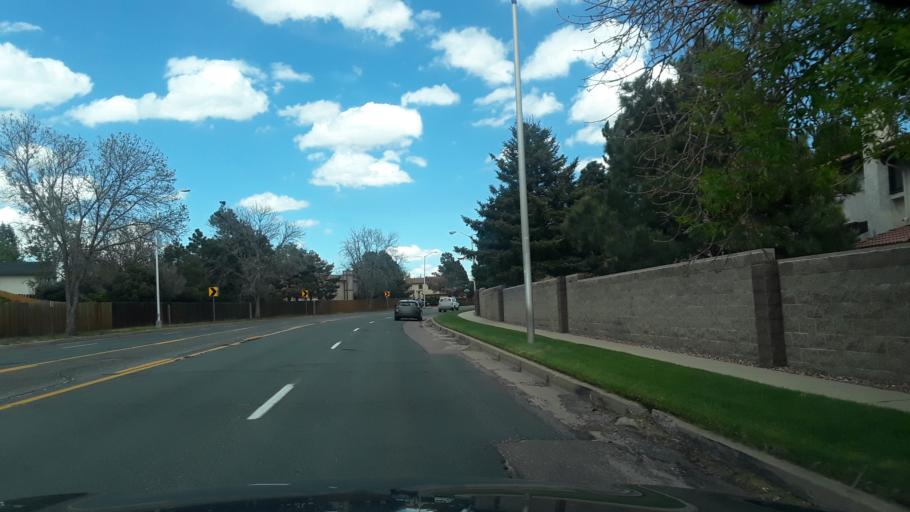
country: US
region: Colorado
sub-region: El Paso County
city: Black Forest
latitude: 38.9421
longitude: -104.7711
